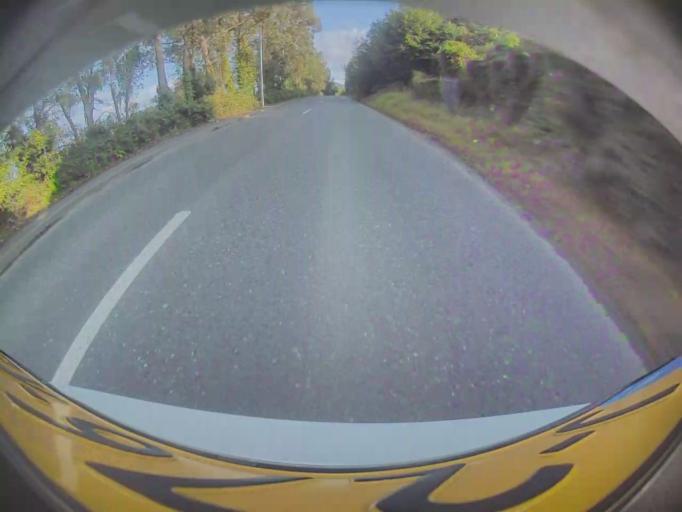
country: IE
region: Leinster
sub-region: Wicklow
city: Enniskerry
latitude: 53.2098
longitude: -6.1750
